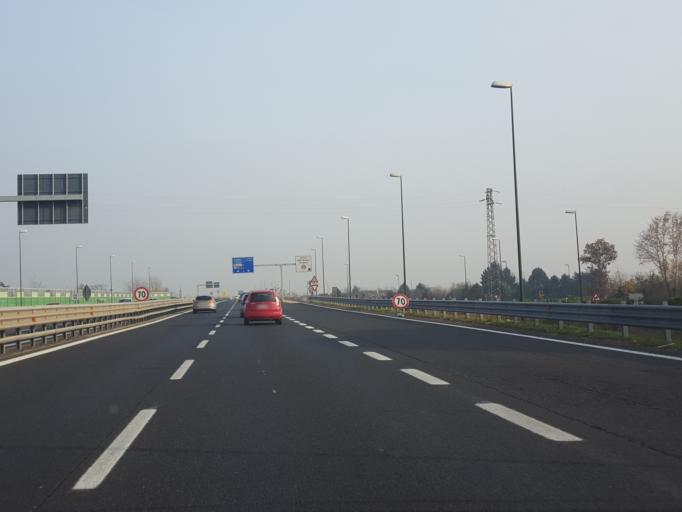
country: IT
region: Veneto
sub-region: Provincia di Treviso
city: Treviso
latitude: 45.6517
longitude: 12.2251
